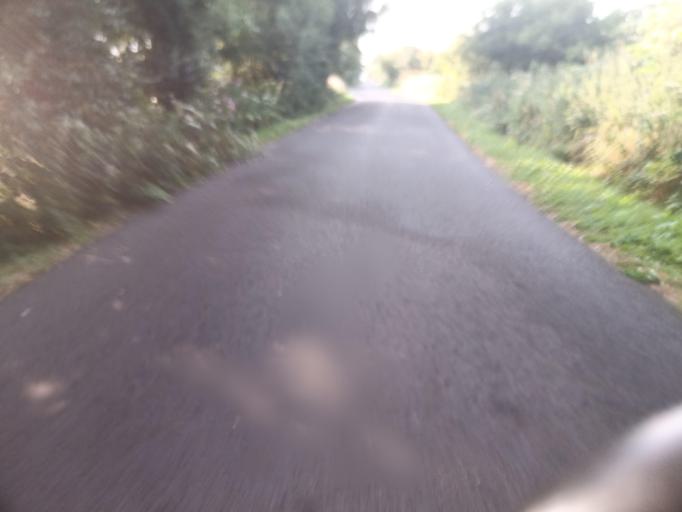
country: GB
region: Northern Ireland
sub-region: Castlereagh District
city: Dundonald
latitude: 54.5796
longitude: -5.7867
